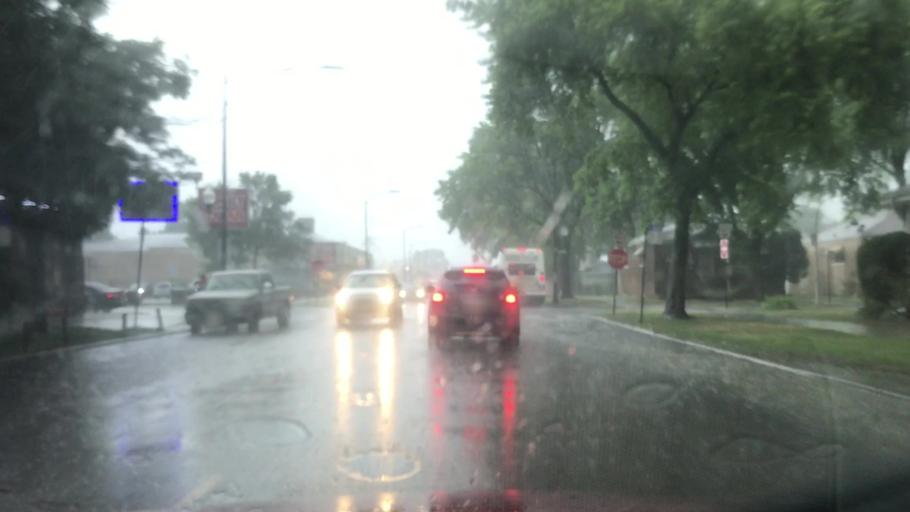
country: US
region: Illinois
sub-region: Cook County
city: Oak Park
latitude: 41.8781
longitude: -87.7549
